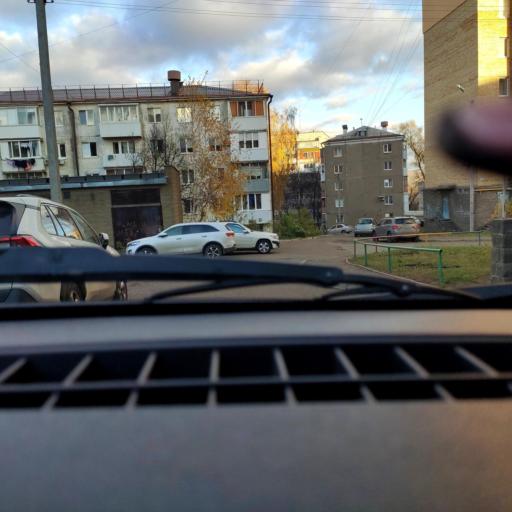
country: RU
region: Bashkortostan
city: Ufa
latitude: 54.7926
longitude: 56.0464
